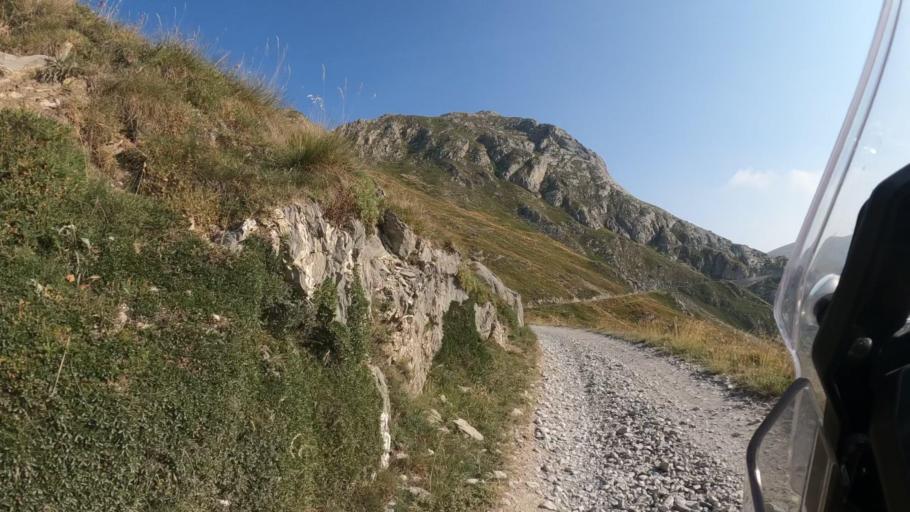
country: IT
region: Piedmont
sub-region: Provincia di Cuneo
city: Limone Piemonte
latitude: 44.1684
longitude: 7.6331
